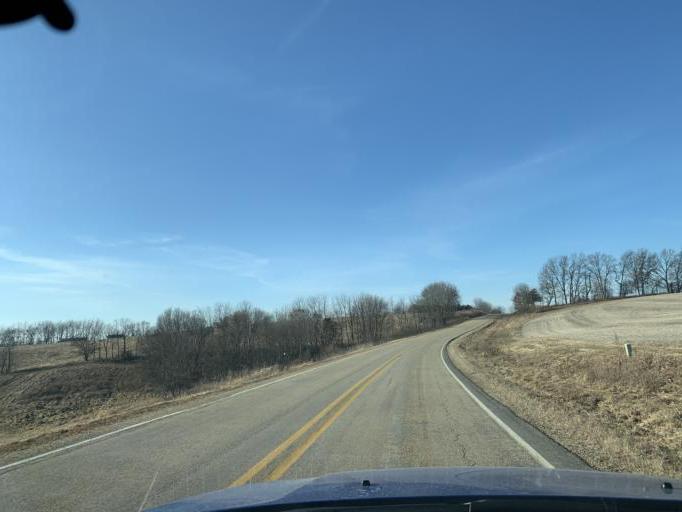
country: US
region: Wisconsin
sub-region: Iowa County
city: Barneveld
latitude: 42.8099
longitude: -89.8903
